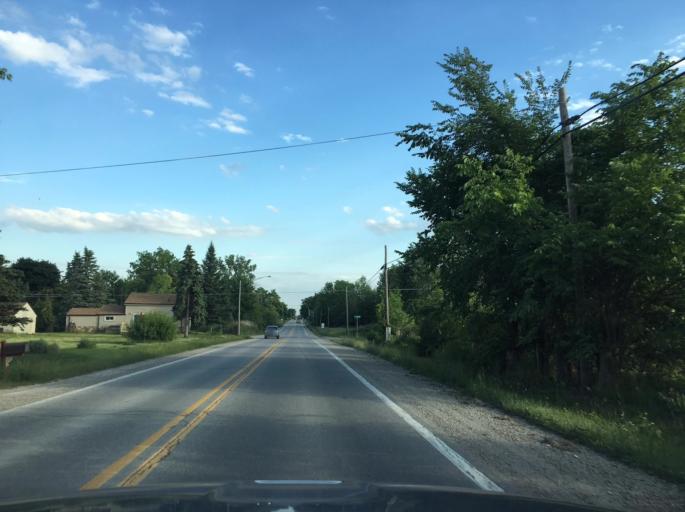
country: US
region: Michigan
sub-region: Macomb County
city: Romeo
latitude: 42.7758
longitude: -82.9616
